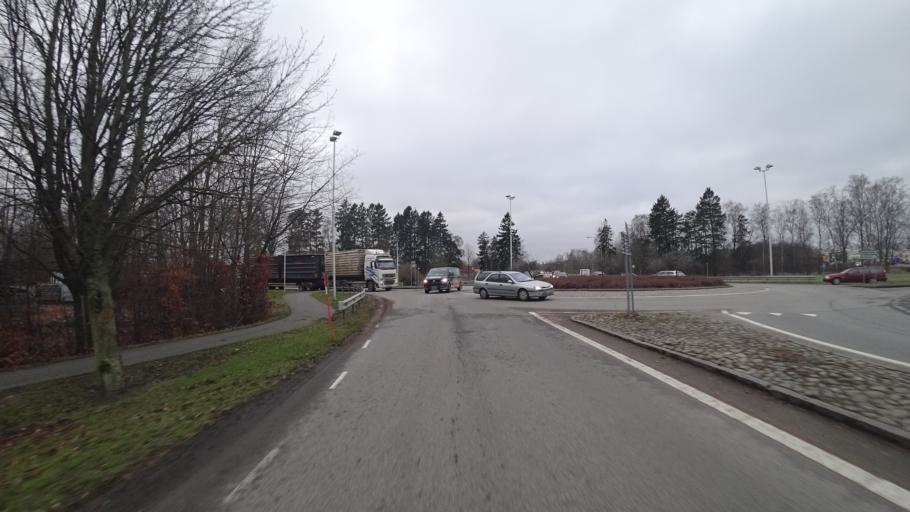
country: SE
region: Skane
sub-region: Kristianstads Kommun
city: Kristianstad
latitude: 56.0430
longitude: 14.1519
